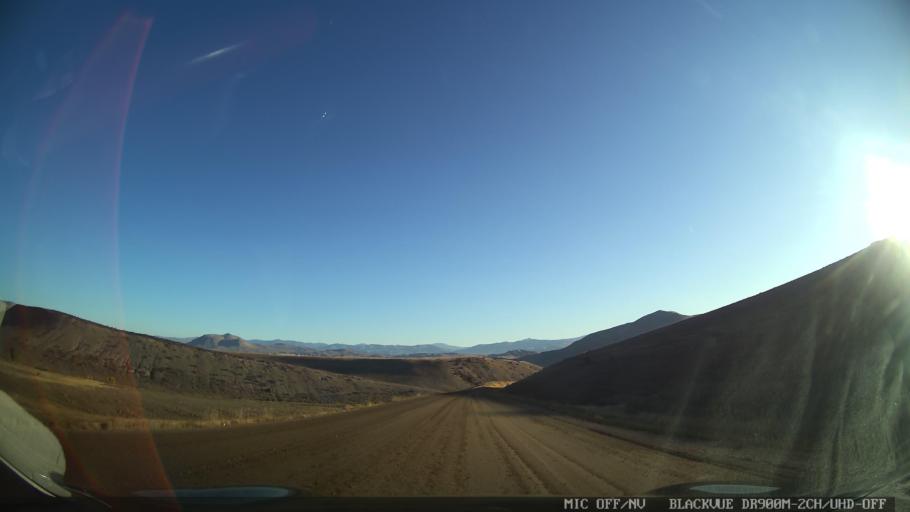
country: US
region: Colorado
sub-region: Grand County
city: Kremmling
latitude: 40.0104
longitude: -106.4009
